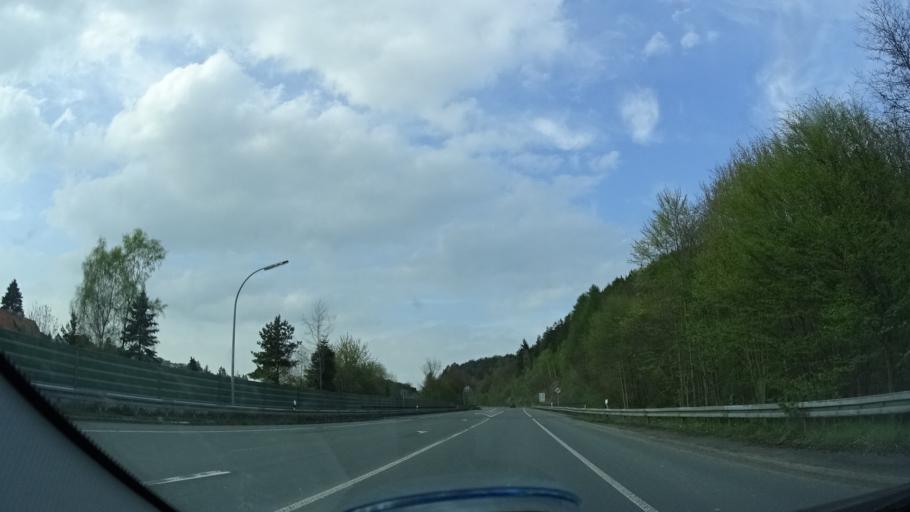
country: DE
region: North Rhine-Westphalia
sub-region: Regierungsbezirk Arnsberg
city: Ruthen
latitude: 51.4882
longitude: 8.4468
